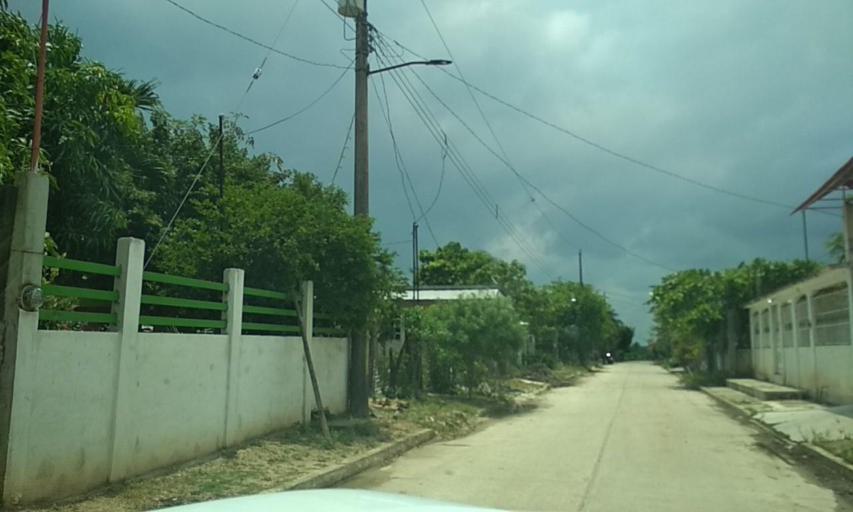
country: MX
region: Veracruz
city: Las Choapas
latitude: 17.8918
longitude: -94.0968
